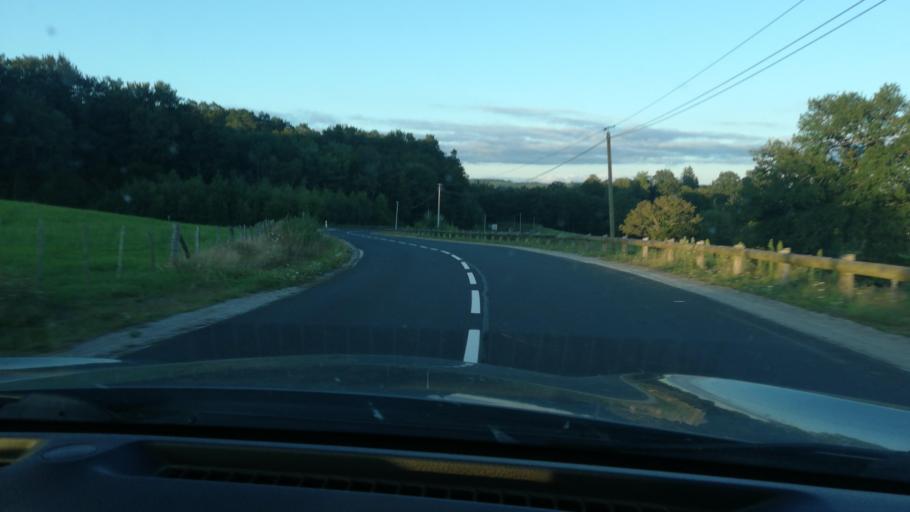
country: FR
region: Auvergne
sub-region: Departement du Cantal
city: Laroquebrou
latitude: 44.9218
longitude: 2.0704
